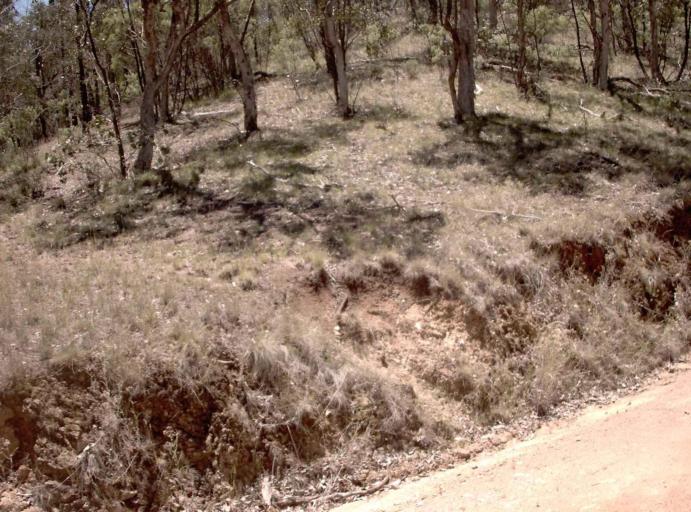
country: AU
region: New South Wales
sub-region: Snowy River
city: Jindabyne
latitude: -36.9255
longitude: 148.3769
